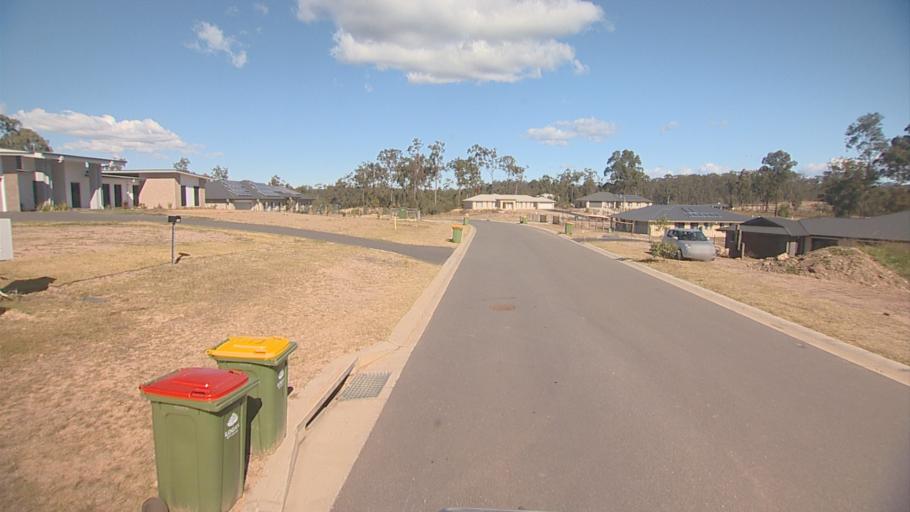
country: AU
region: Queensland
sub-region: Logan
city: North Maclean
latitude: -27.7588
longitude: 152.9342
